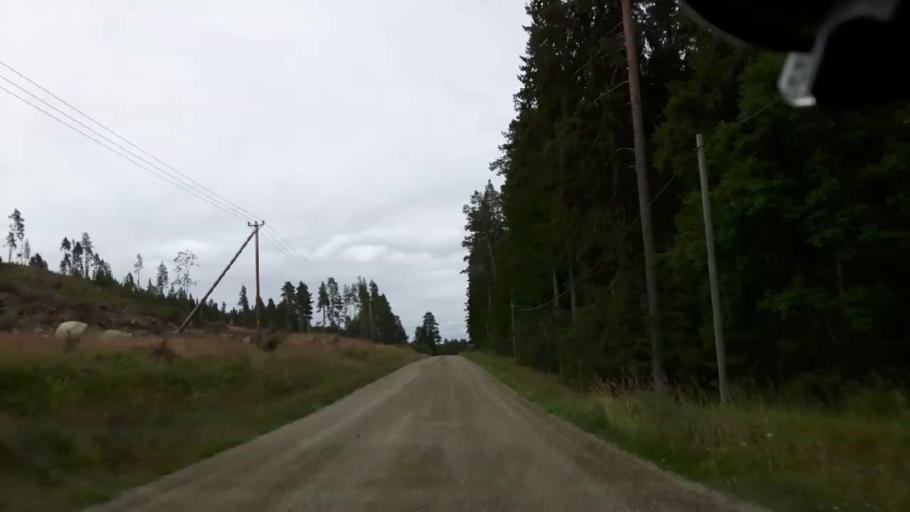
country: SE
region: Jaemtland
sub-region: Braecke Kommun
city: Braecke
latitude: 63.0421
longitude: 15.3569
